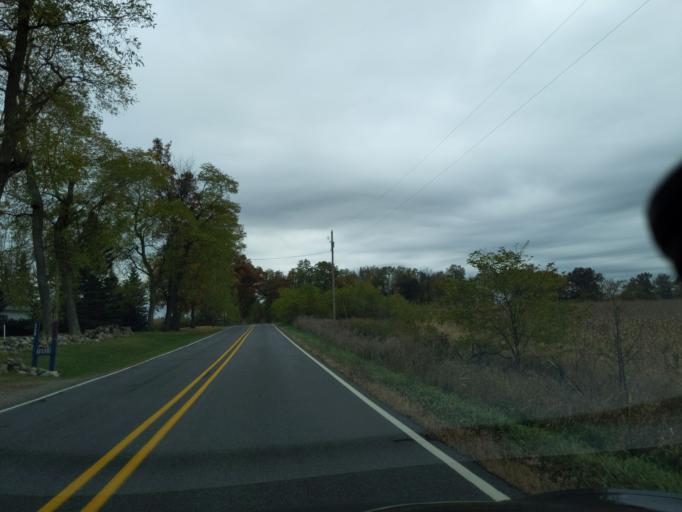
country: US
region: Michigan
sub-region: Eaton County
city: Eaton Rapids
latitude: 42.3922
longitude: -84.6004
